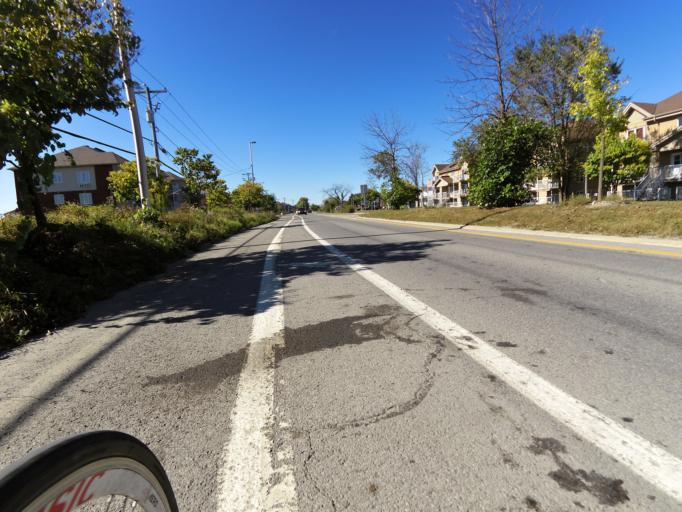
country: CA
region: Ontario
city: Clarence-Rockland
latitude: 45.5245
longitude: -75.4847
